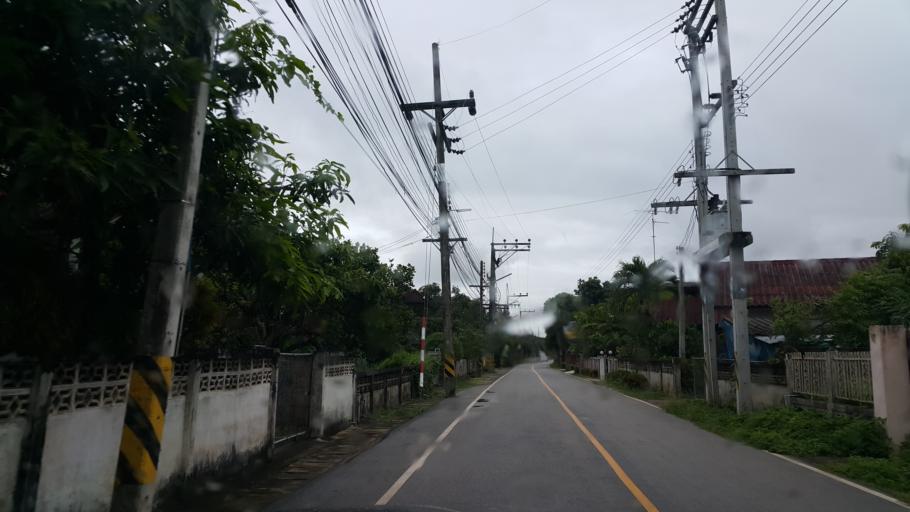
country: TH
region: Phayao
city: Chiang Kham
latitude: 19.5343
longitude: 100.2947
